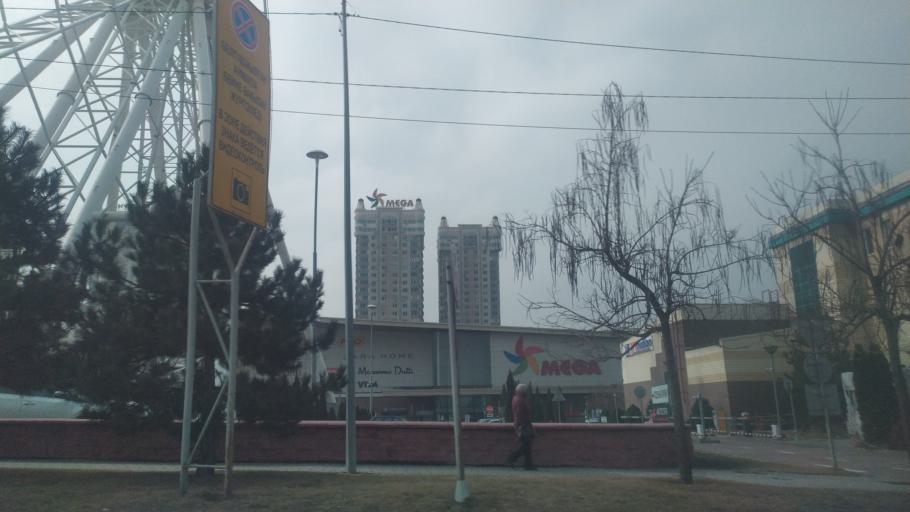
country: KZ
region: Almaty Qalasy
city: Almaty
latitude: 43.2012
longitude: 76.8943
